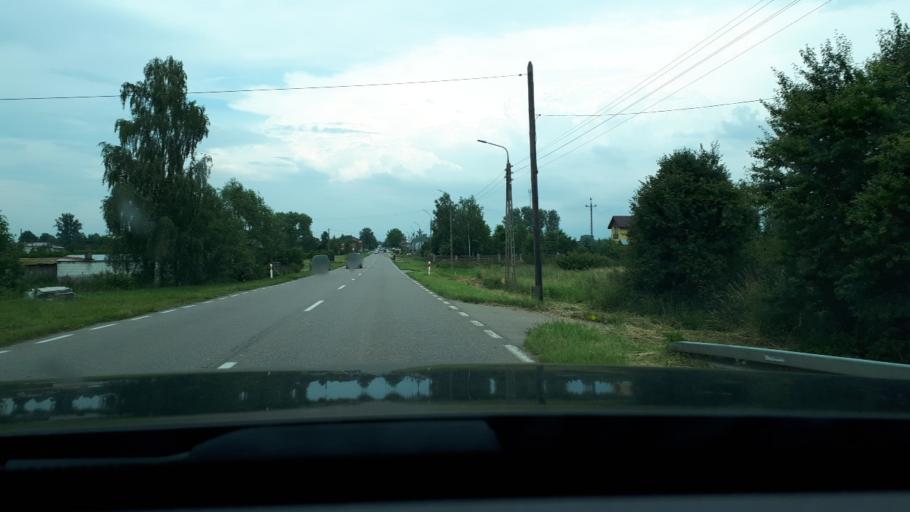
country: PL
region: Podlasie
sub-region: Powiat moniecki
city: Knyszyn
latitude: 53.3060
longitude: 22.9068
